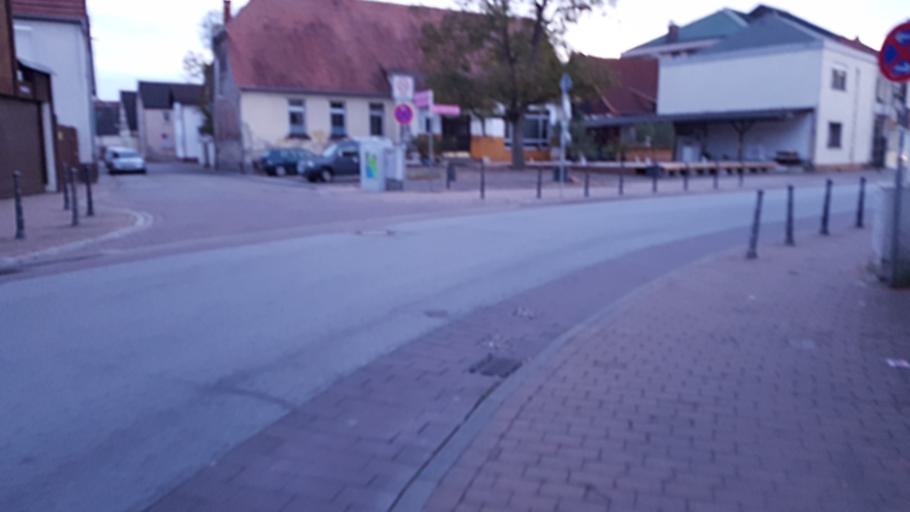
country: DE
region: Hesse
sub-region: Regierungsbezirk Darmstadt
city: Biblis
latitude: 49.6857
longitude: 8.4531
